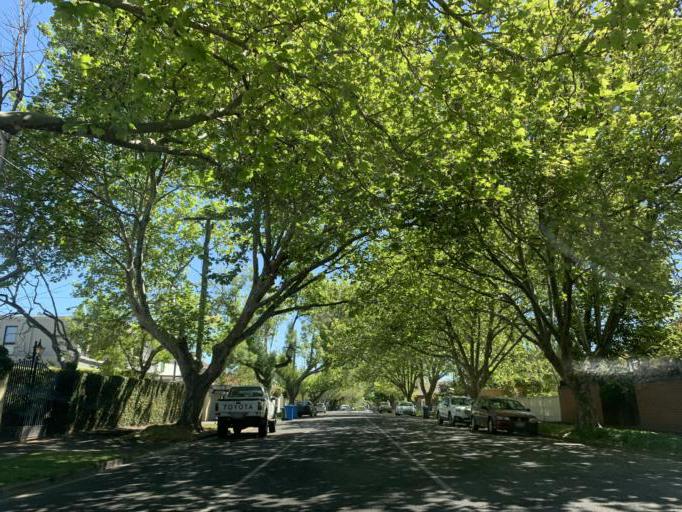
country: AU
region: Victoria
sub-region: Bayside
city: Hampton
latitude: -37.9252
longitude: 144.9962
